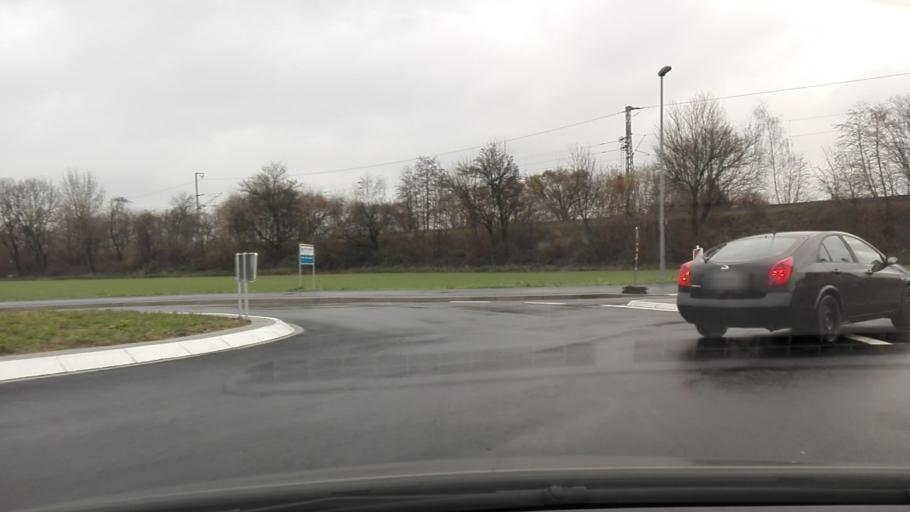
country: DE
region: North Rhine-Westphalia
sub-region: Regierungsbezirk Arnsberg
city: Unna
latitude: 51.5453
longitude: 7.6693
